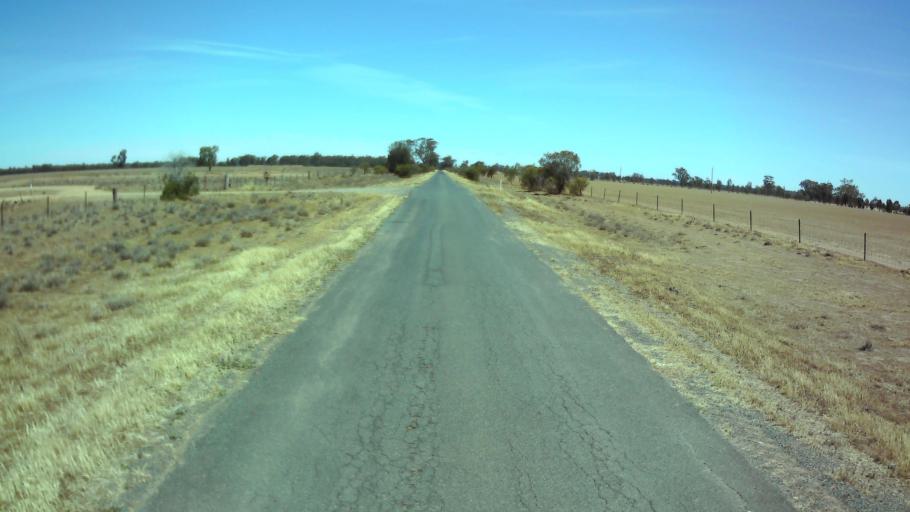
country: AU
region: New South Wales
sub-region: Weddin
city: Grenfell
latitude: -33.8916
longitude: 147.6881
